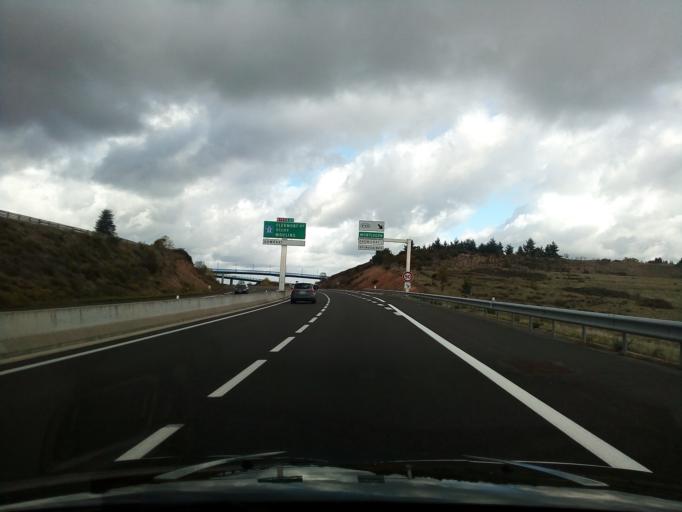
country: FR
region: Auvergne
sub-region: Departement de l'Allier
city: Premilhat
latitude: 46.3303
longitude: 2.5367
